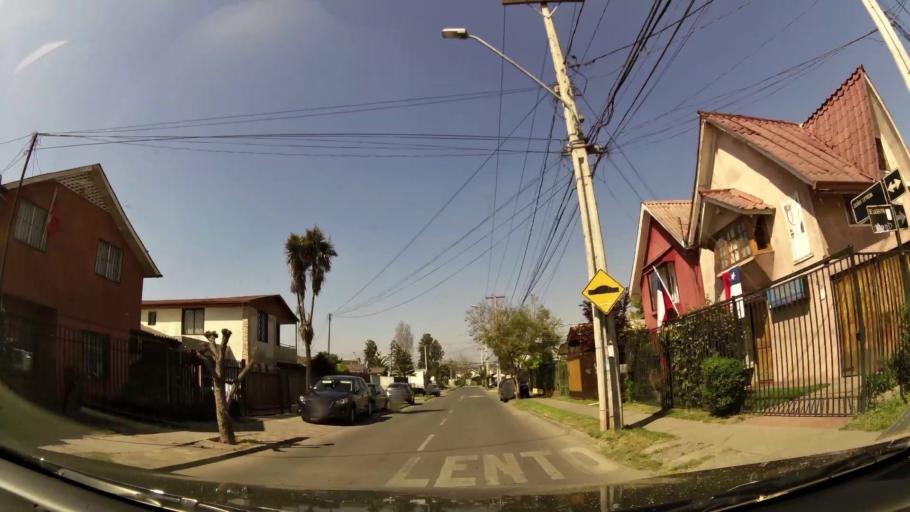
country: CL
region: Santiago Metropolitan
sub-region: Provincia de Santiago
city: Lo Prado
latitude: -33.3631
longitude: -70.7251
